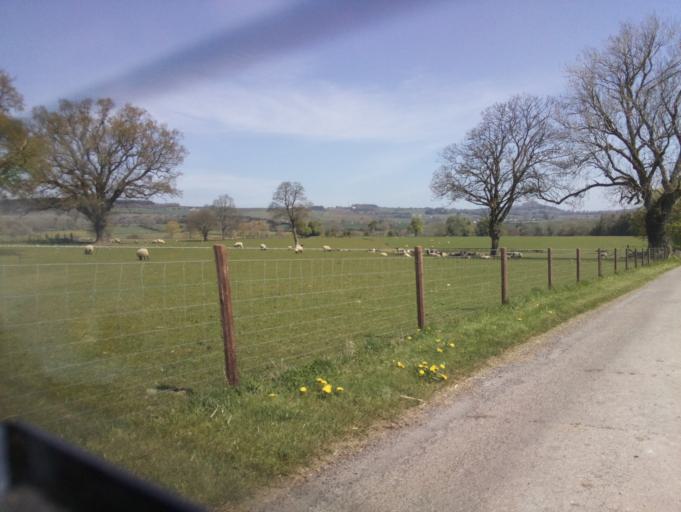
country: GB
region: Wales
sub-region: Monmouthshire
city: Chepstow
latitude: 51.6511
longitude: -2.7298
